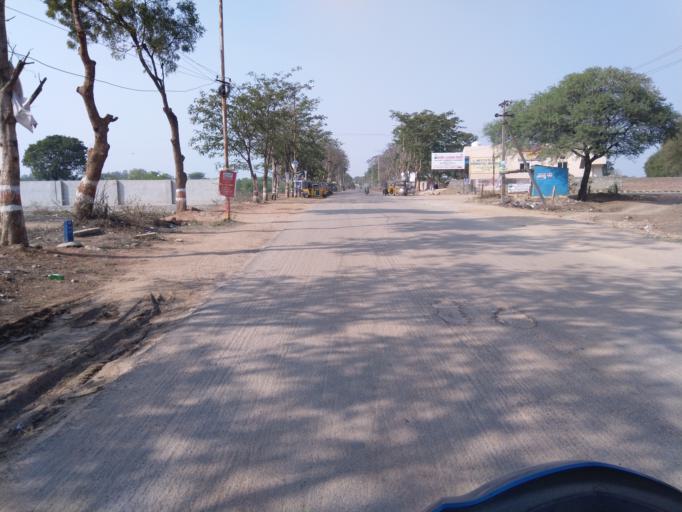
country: IN
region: Telangana
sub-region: Rangareddi
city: Quthbullapur
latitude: 17.5982
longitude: 78.4163
